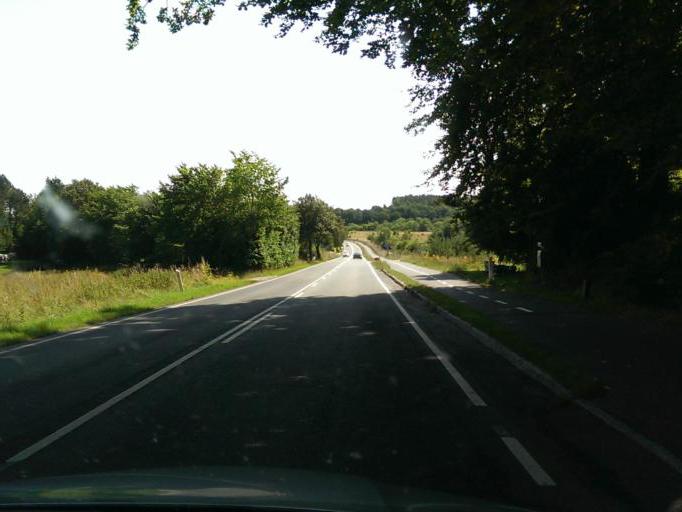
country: DK
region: Central Jutland
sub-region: Syddjurs Kommune
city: Ronde
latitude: 56.2424
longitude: 10.5645
